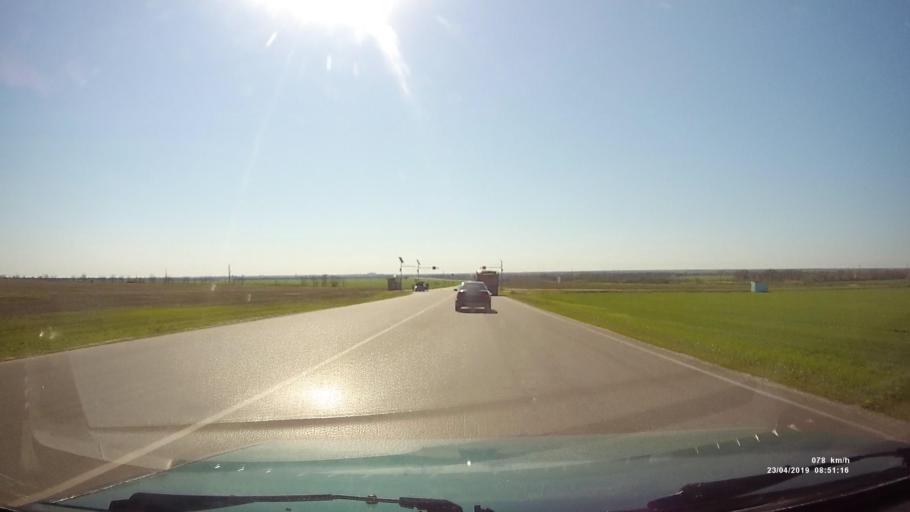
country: RU
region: Rostov
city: Gigant
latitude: 46.4903
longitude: 41.4399
